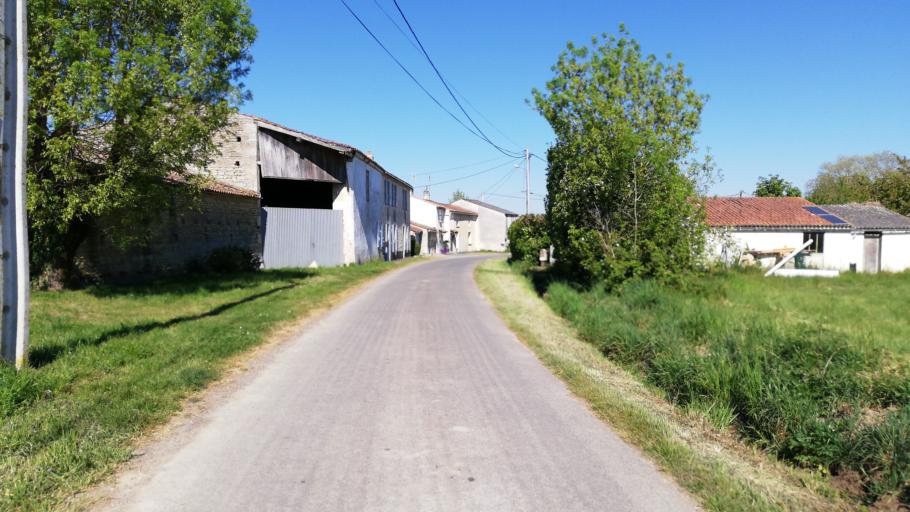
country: FR
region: Pays de la Loire
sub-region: Departement de la Vendee
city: Maillezais
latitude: 46.3274
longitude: -0.7489
